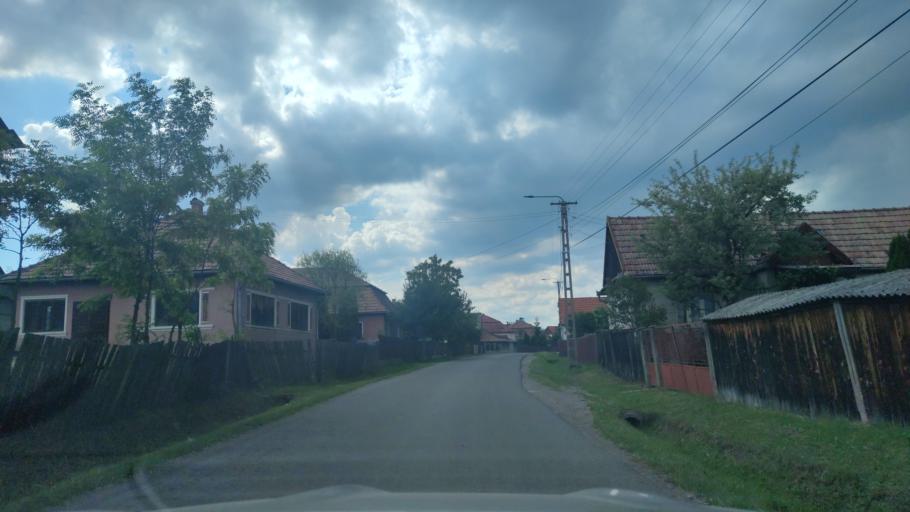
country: RO
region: Harghita
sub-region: Comuna Remetea
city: Remetea
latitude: 46.7997
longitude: 25.4531
